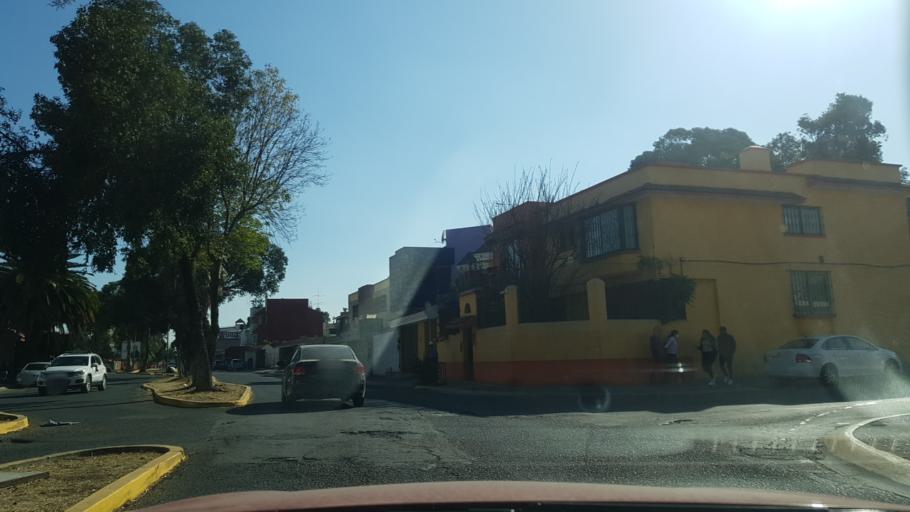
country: MX
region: Mexico
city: Cuautitlan Izcalli
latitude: 19.6417
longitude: -99.1999
